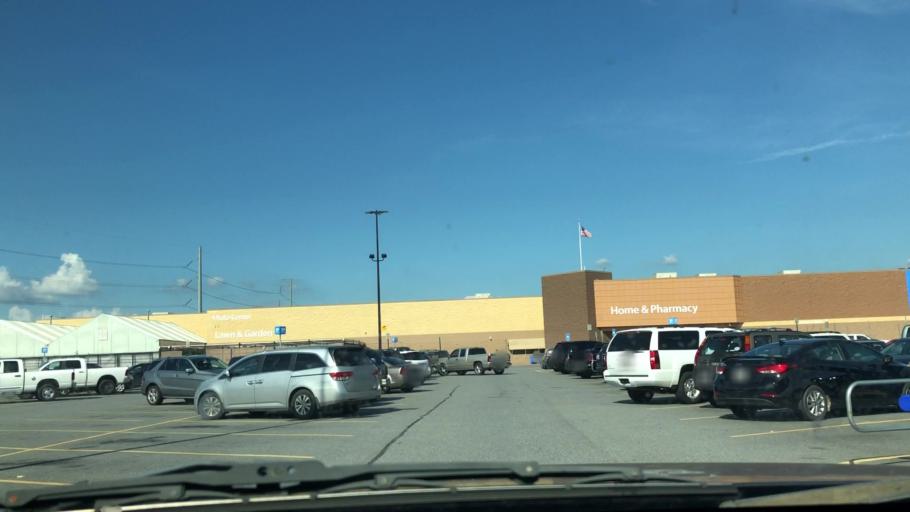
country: US
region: Georgia
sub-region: Bartow County
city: Cartersville
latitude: 34.2029
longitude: -84.7892
